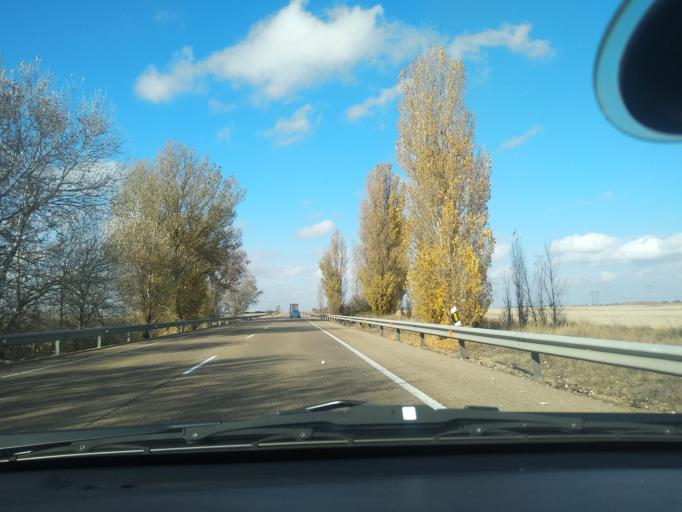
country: ES
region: Castille and Leon
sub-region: Provincia de Valladolid
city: Valdenebro de los Valles
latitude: 41.8053
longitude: -4.9718
